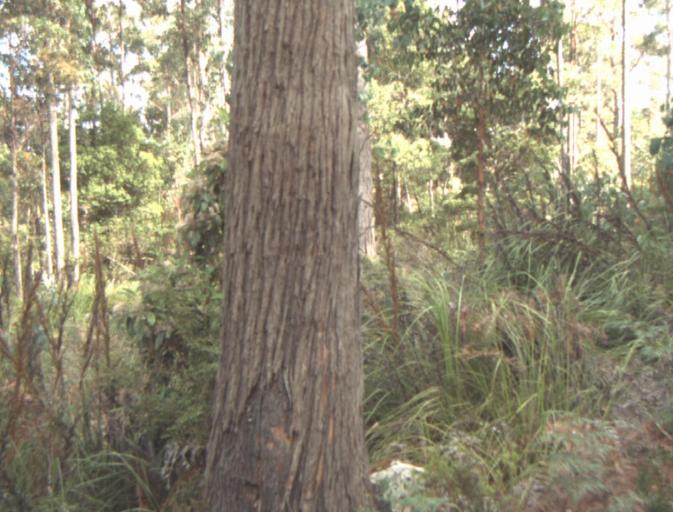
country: AU
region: Tasmania
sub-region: Launceston
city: Mayfield
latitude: -41.2910
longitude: 147.2401
